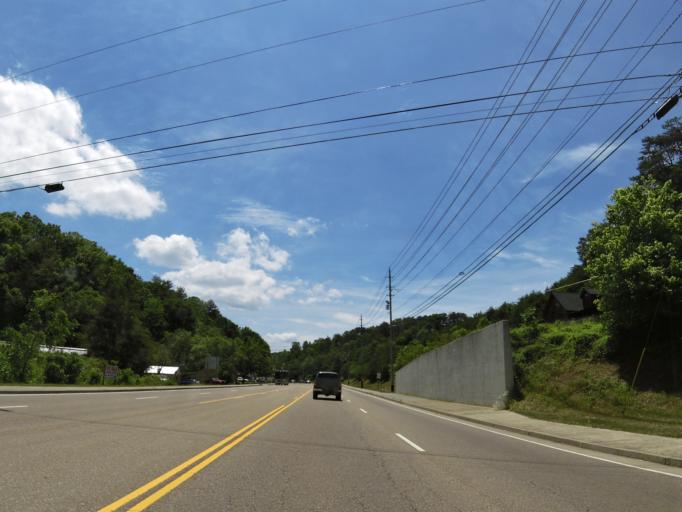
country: US
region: Tennessee
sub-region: Sevier County
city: Pigeon Forge
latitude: 35.8024
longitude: -83.5400
